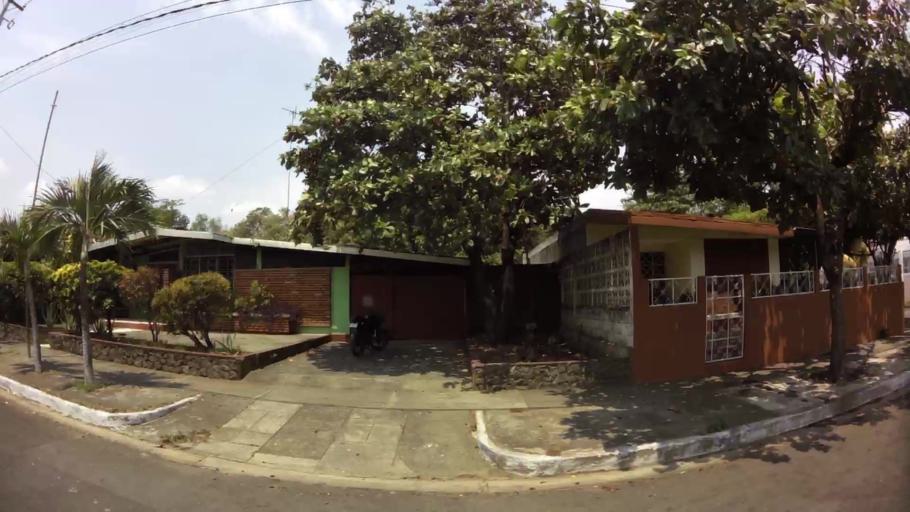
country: NI
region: Managua
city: Ciudad Sandino
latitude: 12.1529
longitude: -86.3114
